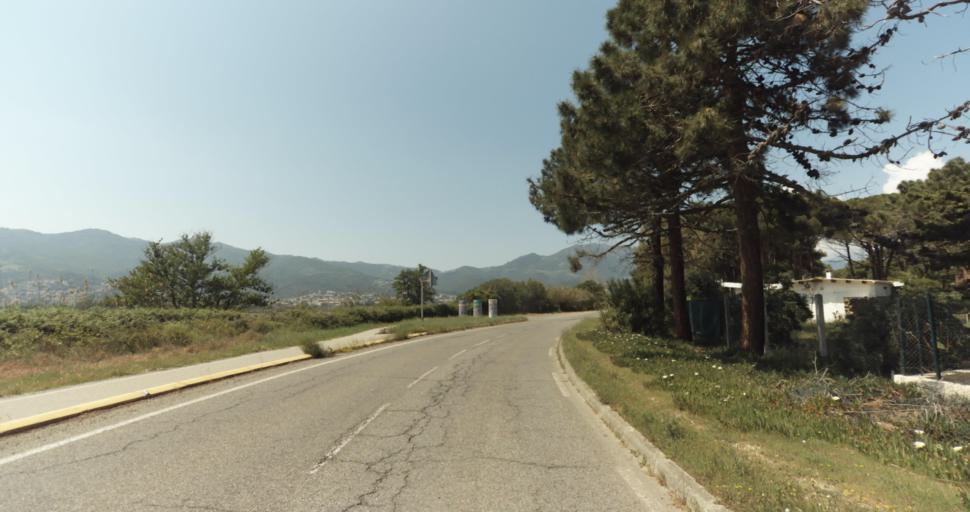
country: FR
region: Corsica
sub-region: Departement de la Haute-Corse
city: Biguglia
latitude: 42.6428
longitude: 9.4573
